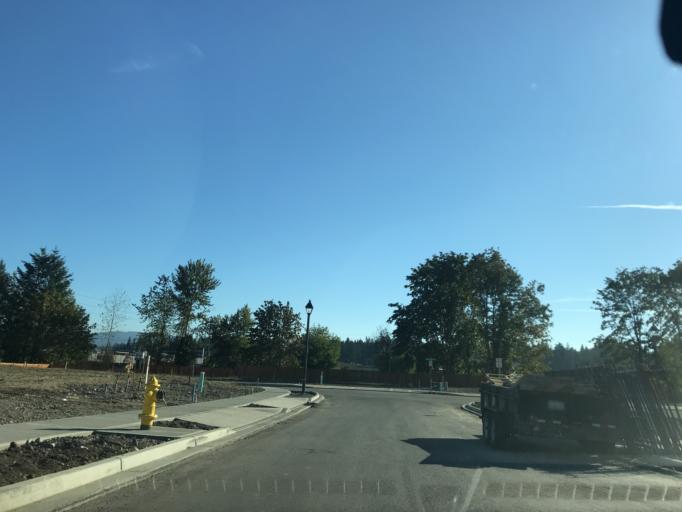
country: US
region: Washington
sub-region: King County
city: Maple Valley
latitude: 47.3599
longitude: -122.0240
